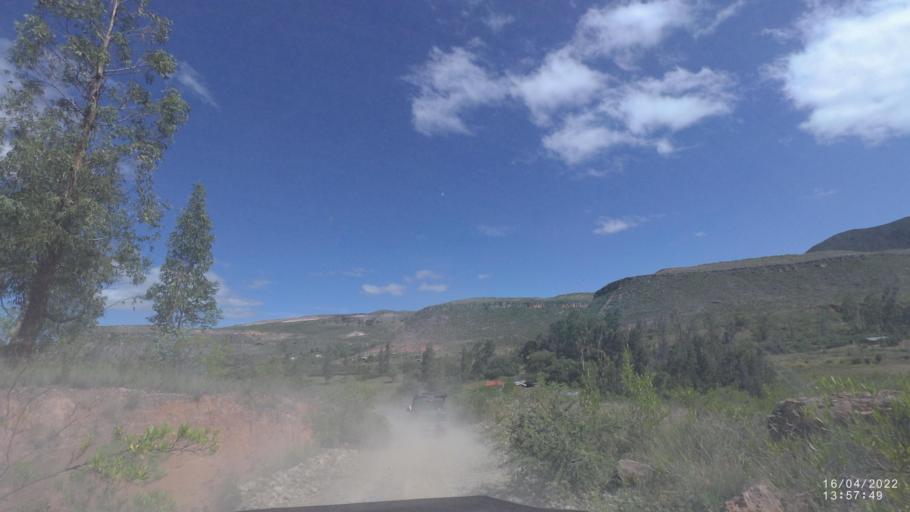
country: BO
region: Cochabamba
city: Mizque
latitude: -18.0386
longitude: -65.5588
